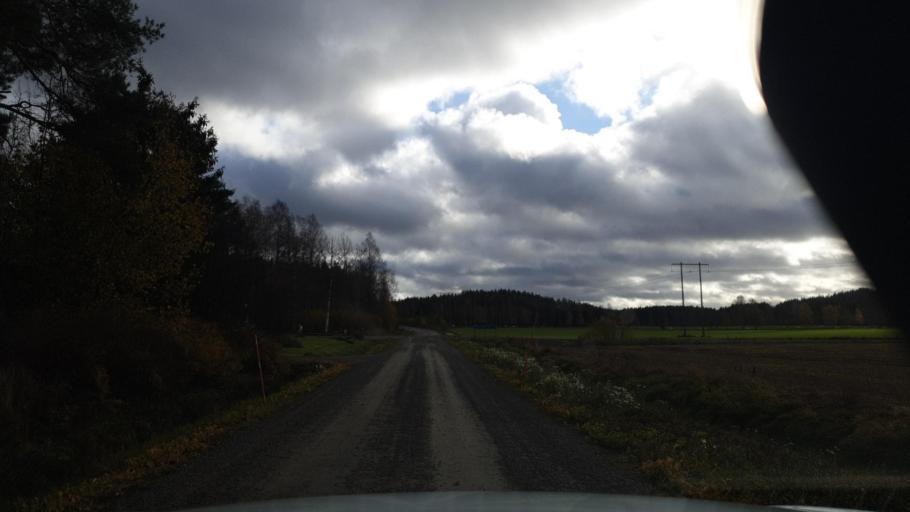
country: SE
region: Vaermland
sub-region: Arvika Kommun
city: Arvika
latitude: 59.4891
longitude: 12.7452
